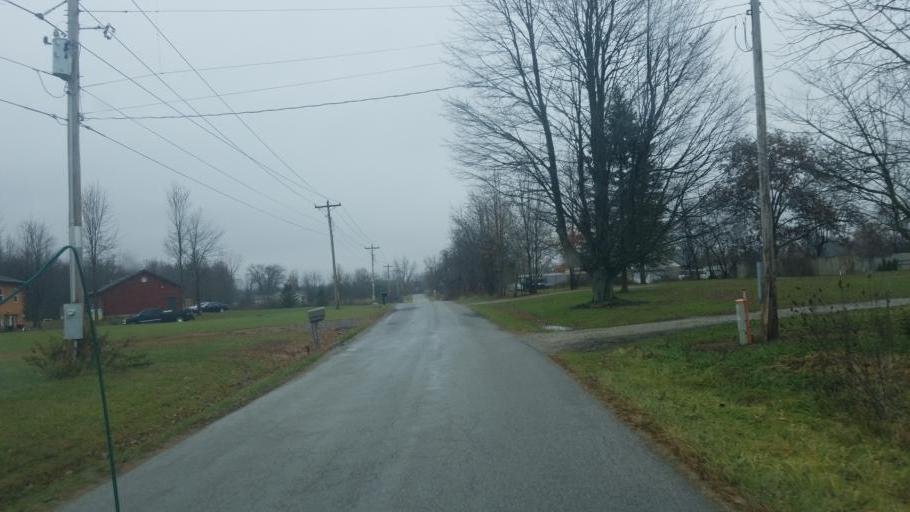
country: US
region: Ohio
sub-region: Morrow County
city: Cardington
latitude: 40.4172
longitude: -82.8402
